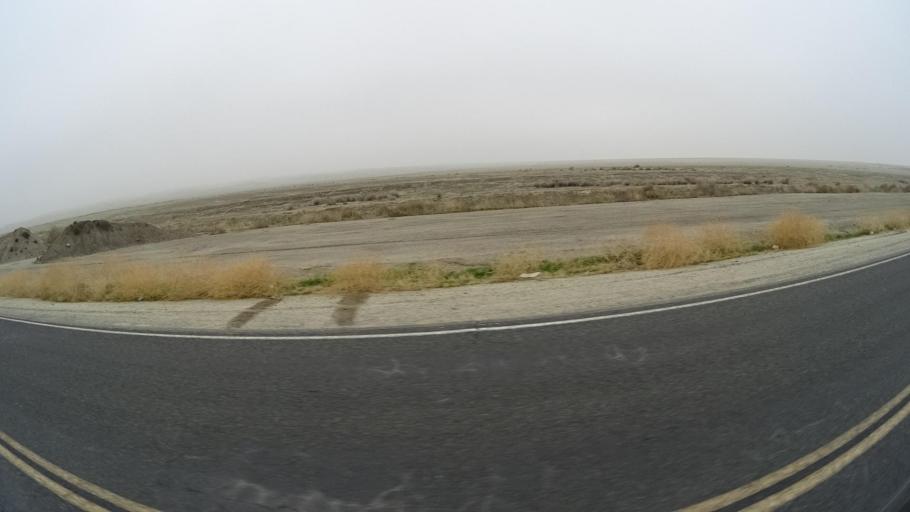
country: US
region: California
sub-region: Kern County
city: Buttonwillow
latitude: 35.3434
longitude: -119.4678
